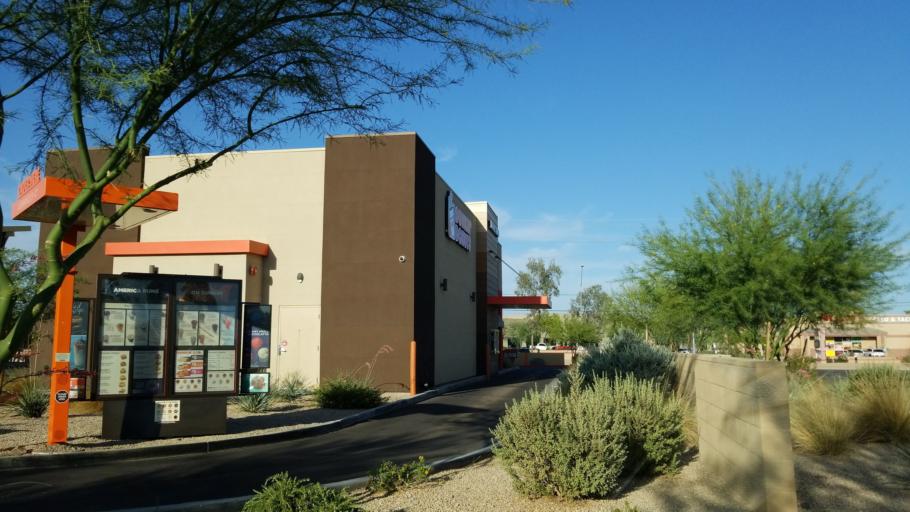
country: US
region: Arizona
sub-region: Maricopa County
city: Paradise Valley
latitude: 33.6787
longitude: -112.0317
